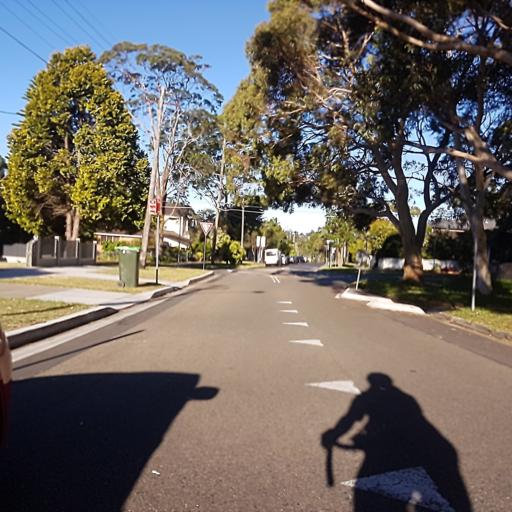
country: AU
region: New South Wales
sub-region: Ku-ring-gai
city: Roseville Chase
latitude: -33.7817
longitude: 151.2011
